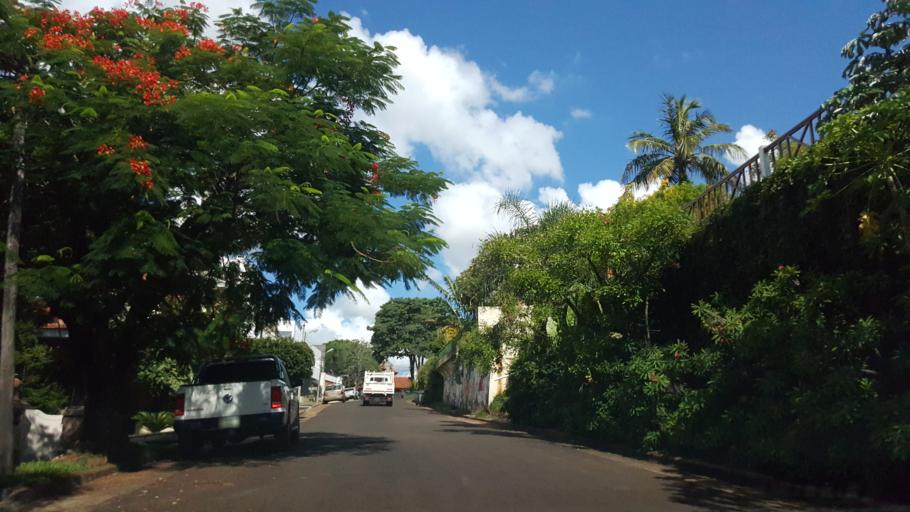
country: AR
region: Misiones
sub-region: Departamento de Capital
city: Posadas
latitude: -27.3531
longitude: -55.8979
